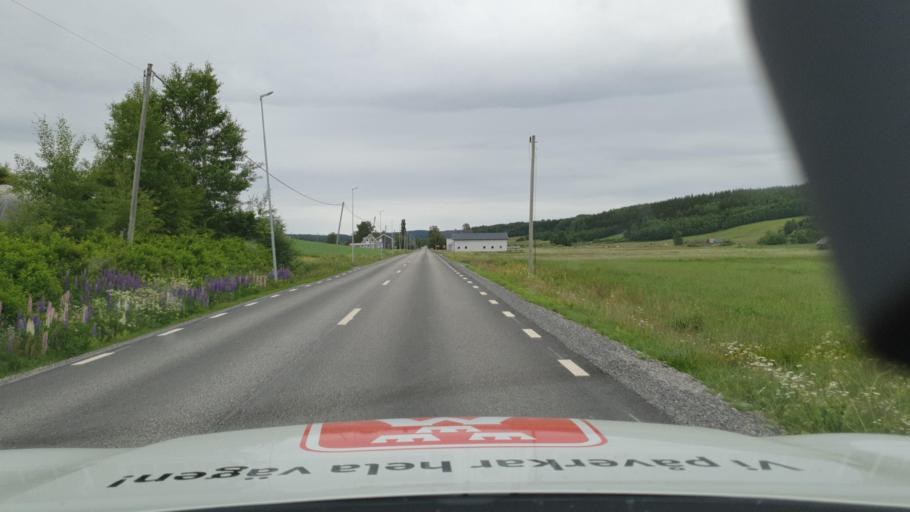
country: SE
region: Vaesterbotten
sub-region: Vannas Kommun
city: Vaennaes
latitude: 63.7631
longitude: 19.6272
